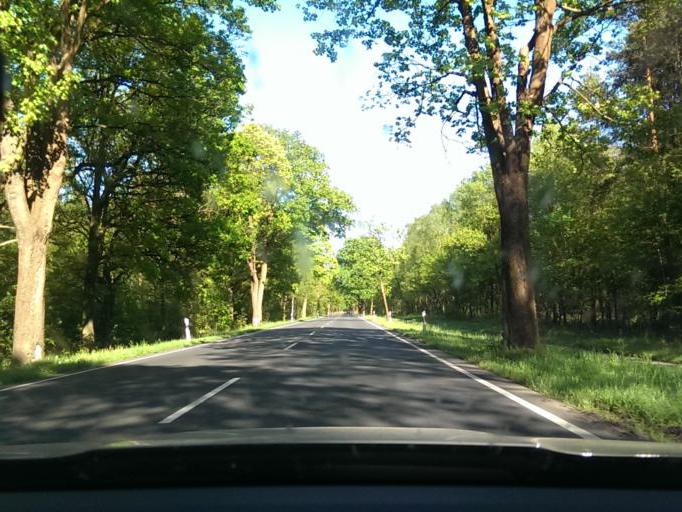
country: DE
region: Lower Saxony
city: Winsen (Aller)
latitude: 52.6346
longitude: 9.8992
